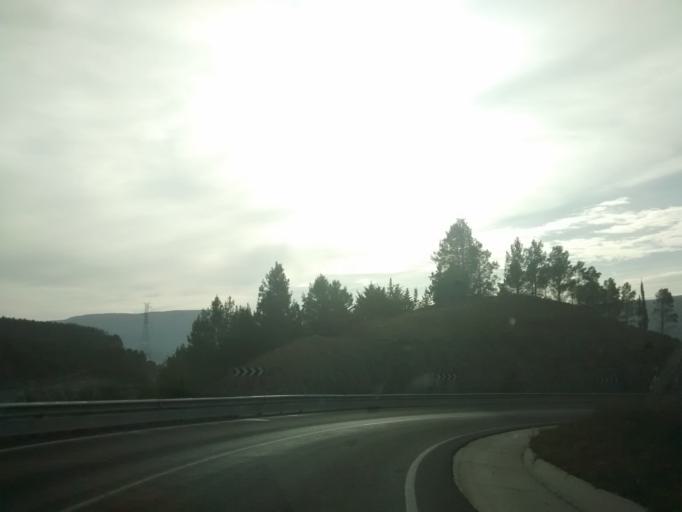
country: ES
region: Aragon
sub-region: Provincia de Zaragoza
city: Undues de Lerda
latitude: 42.6181
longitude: -1.1125
